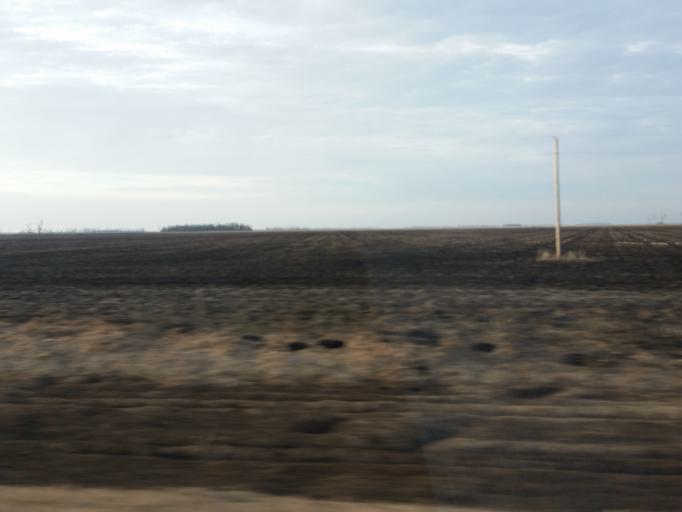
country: US
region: North Dakota
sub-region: Traill County
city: Mayville
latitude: 47.3529
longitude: -97.2779
